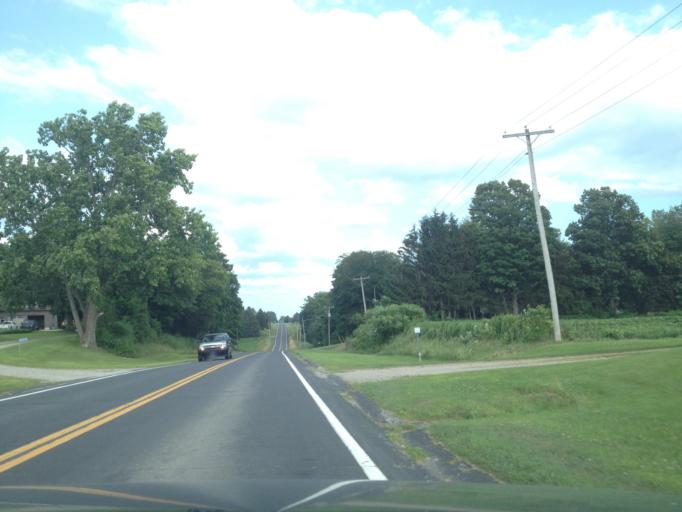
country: CA
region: Ontario
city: Aylmer
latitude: 42.6753
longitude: -80.9569
